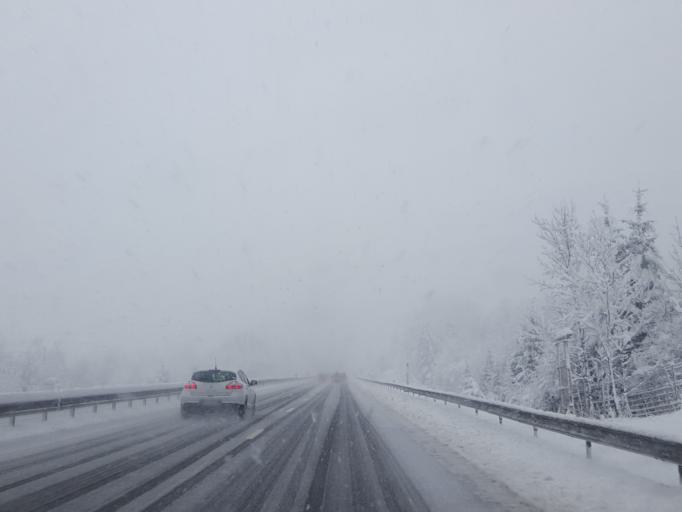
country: FR
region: Rhone-Alpes
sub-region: Departement de la Haute-Savoie
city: Evires
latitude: 46.0402
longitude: 6.2473
